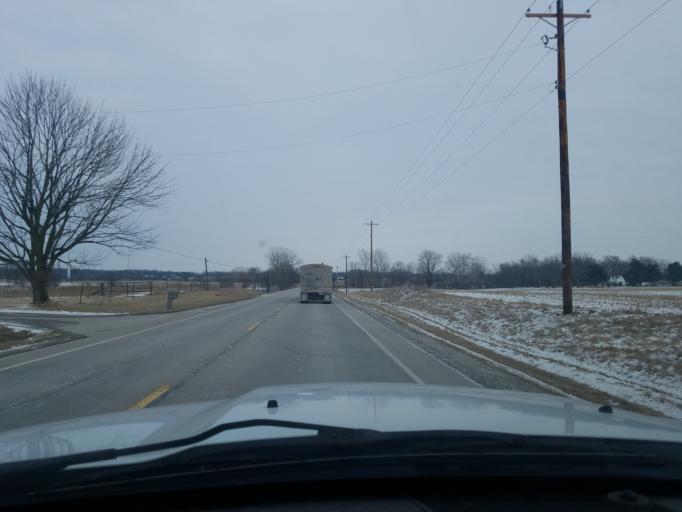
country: US
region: Indiana
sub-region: Randolph County
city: Lynn
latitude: 40.0485
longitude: -84.9725
